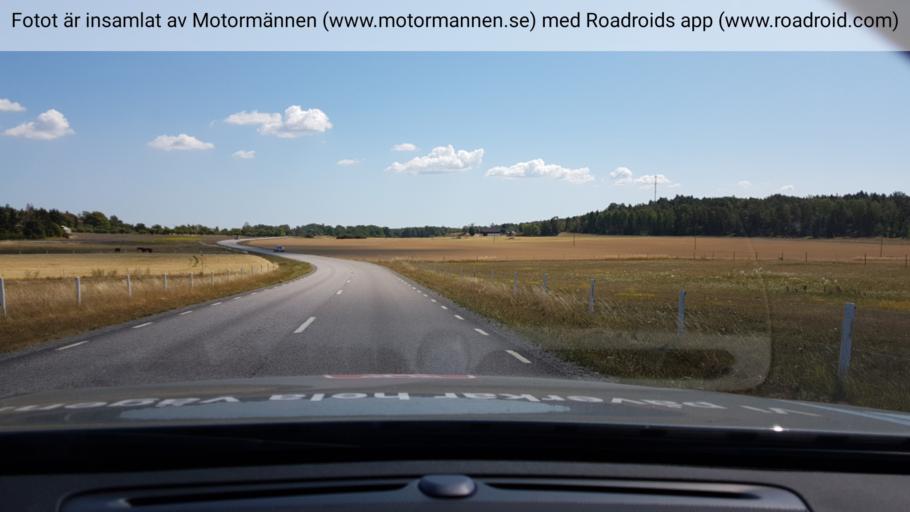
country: SE
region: Stockholm
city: Stenhamra
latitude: 59.3908
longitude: 17.6650
